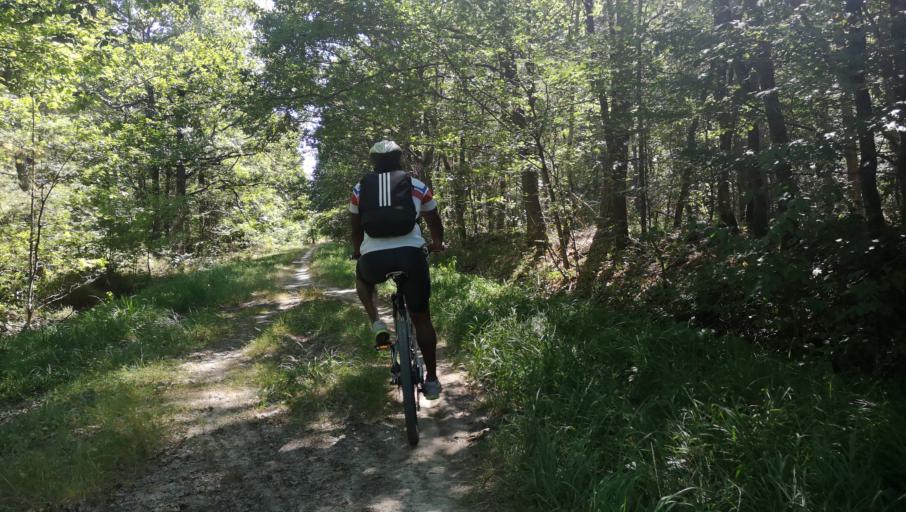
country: FR
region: Centre
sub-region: Departement du Loiret
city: Chanteau
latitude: 47.9591
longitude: 1.9470
